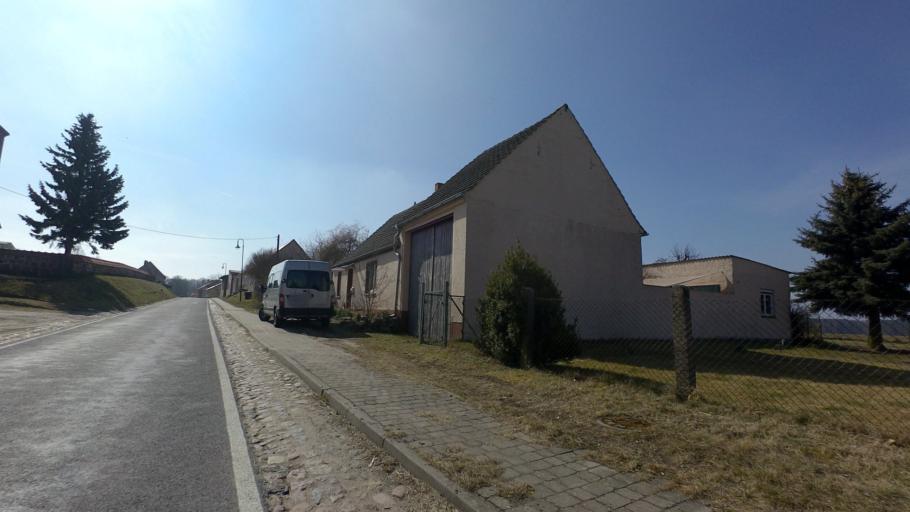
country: DE
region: Brandenburg
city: Wiesenburg
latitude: 52.0376
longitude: 12.5184
